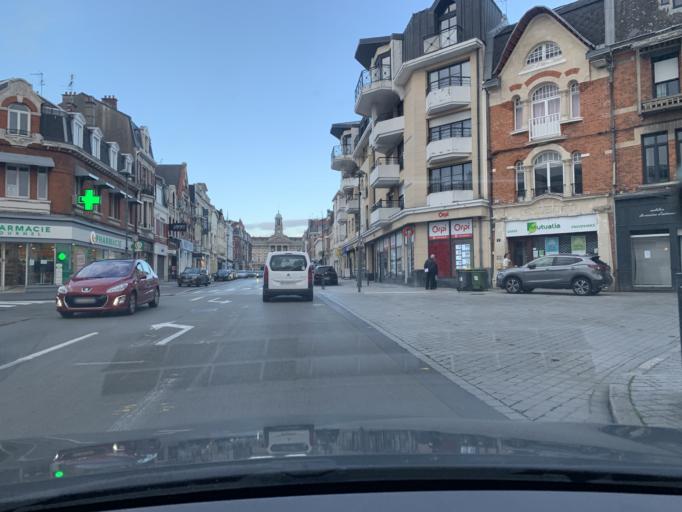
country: FR
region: Nord-Pas-de-Calais
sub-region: Departement du Nord
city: Cambrai
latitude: 50.1735
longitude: 3.2332
